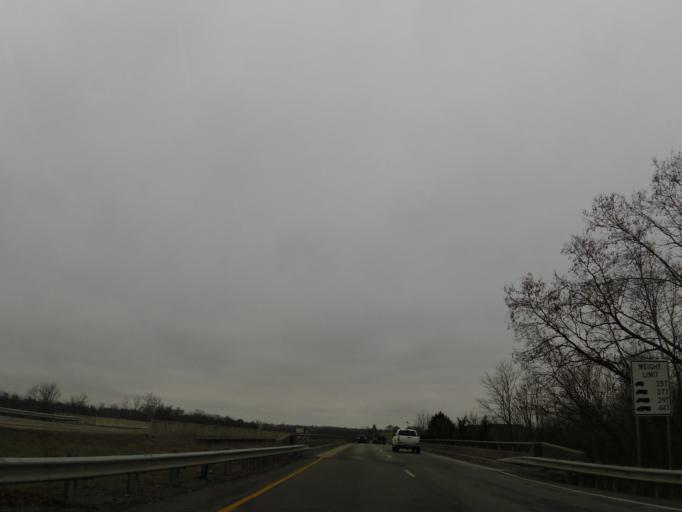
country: US
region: Kentucky
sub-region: Anderson County
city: Lawrenceburg
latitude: 38.0626
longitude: -84.9210
